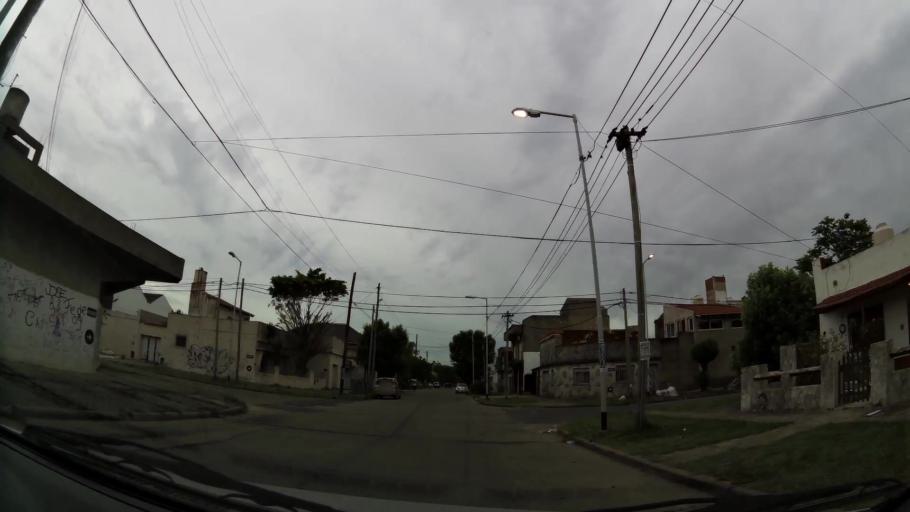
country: AR
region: Buenos Aires
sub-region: Partido de Avellaneda
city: Avellaneda
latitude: -34.6854
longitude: -58.3679
